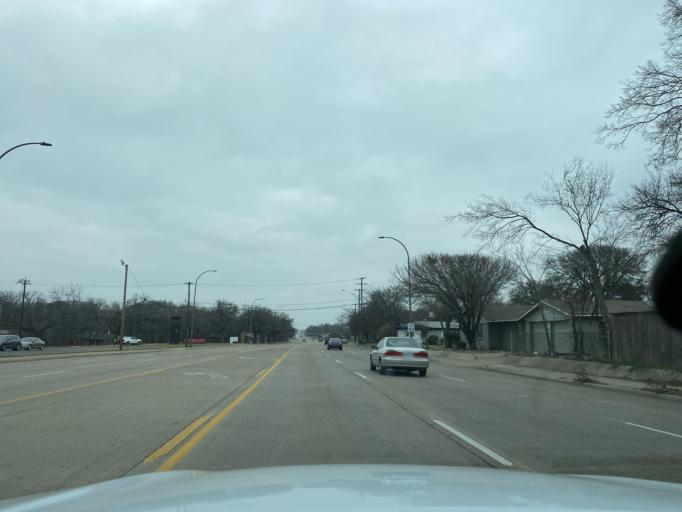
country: US
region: Texas
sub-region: Tarrant County
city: Arlington
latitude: 32.7237
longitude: -97.0974
